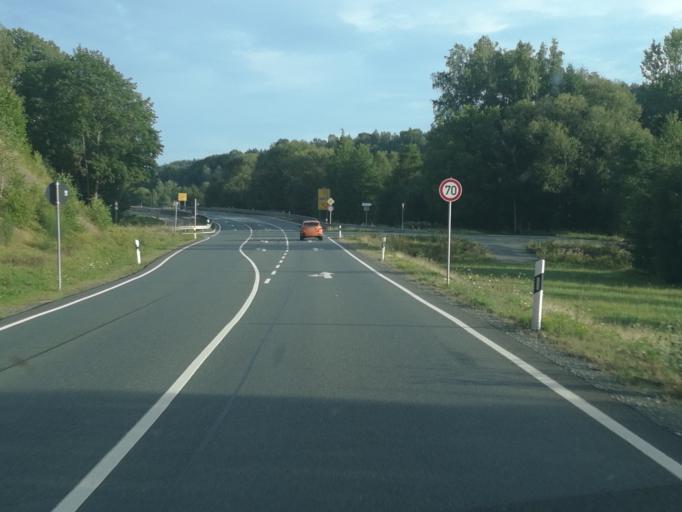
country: DE
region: Saxony
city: Adorf
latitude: 50.3397
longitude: 12.2480
